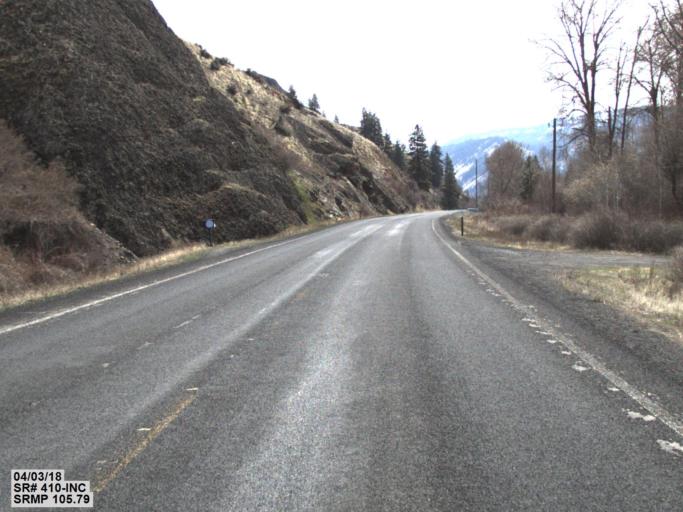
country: US
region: Washington
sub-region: Yakima County
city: Tieton
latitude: 46.8406
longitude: -120.9446
